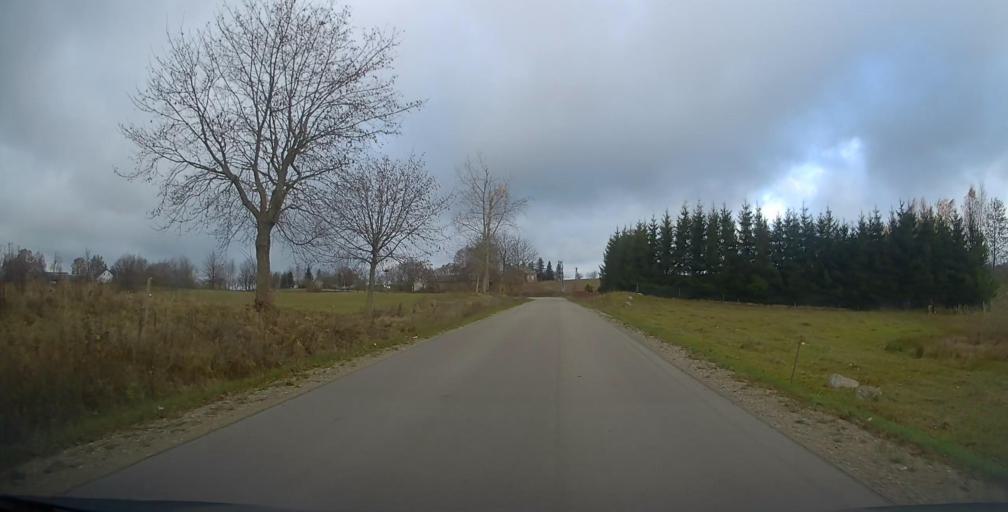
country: PL
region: Podlasie
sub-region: Suwalki
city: Suwalki
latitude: 54.3144
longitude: 22.8777
